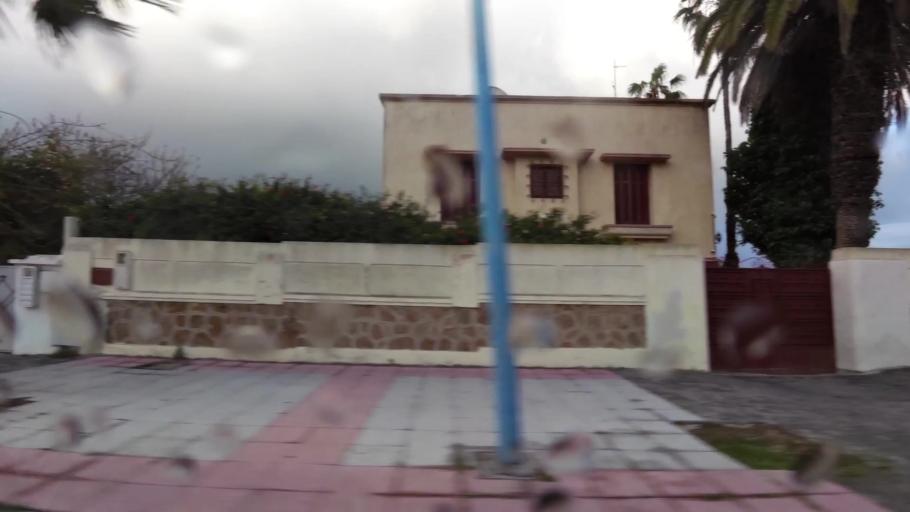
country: MA
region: Doukkala-Abda
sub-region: El-Jadida
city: El Jadida
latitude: 33.2440
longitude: -8.5050
